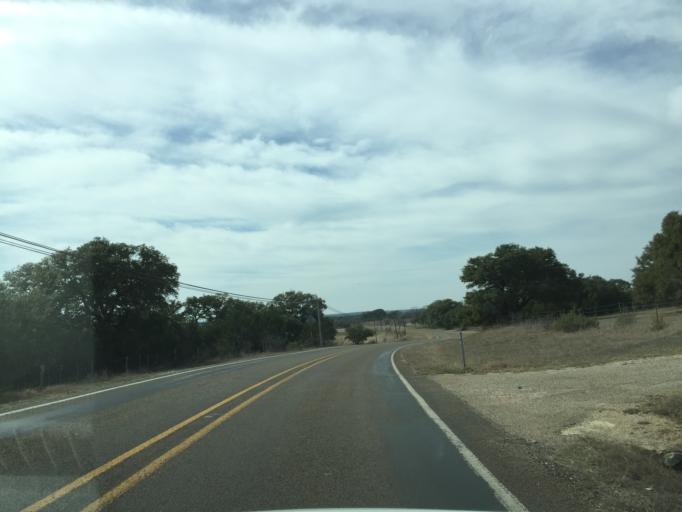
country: US
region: Texas
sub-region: Gillespie County
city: Fredericksburg
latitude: 30.4008
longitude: -98.7046
